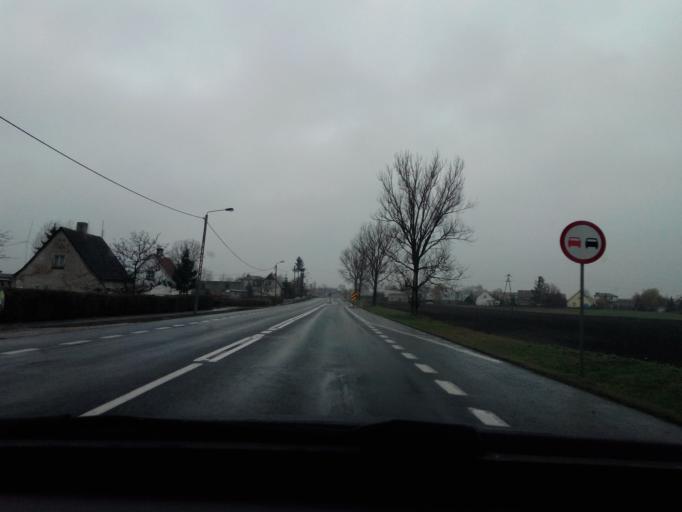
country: PL
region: Pomeranian Voivodeship
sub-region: Powiat tczewski
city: Gniew
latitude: 53.9018
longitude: 18.7850
